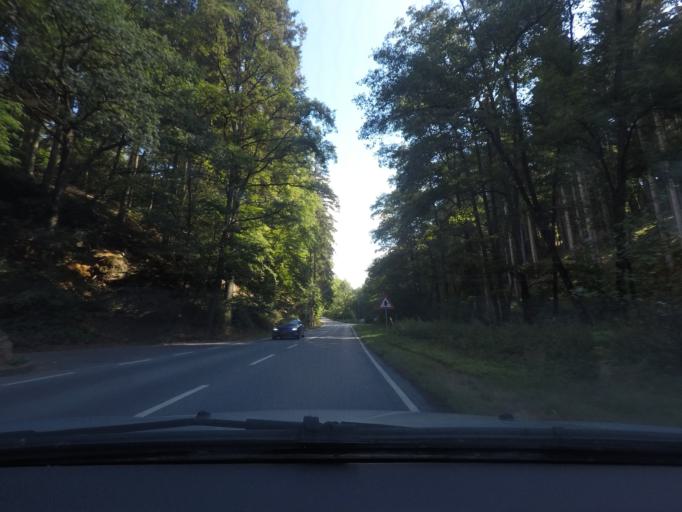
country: LU
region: Luxembourg
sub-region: Canton de Mersch
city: Heffingen
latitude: 49.7488
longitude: 6.2664
